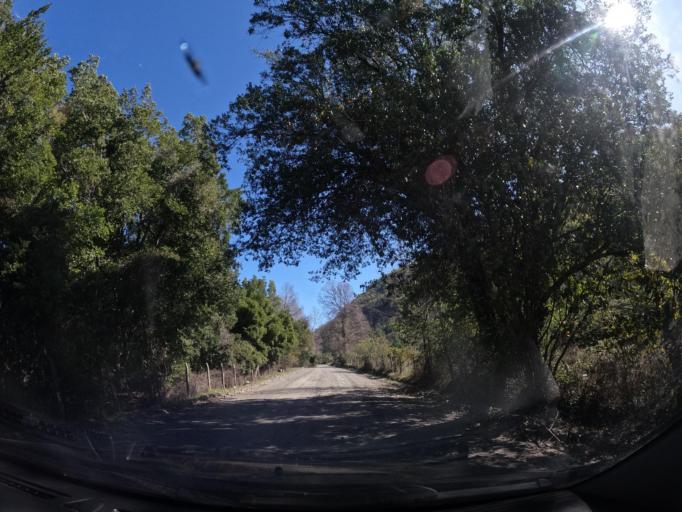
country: CL
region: Maule
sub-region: Provincia de Linares
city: Longavi
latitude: -36.2281
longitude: -71.3934
